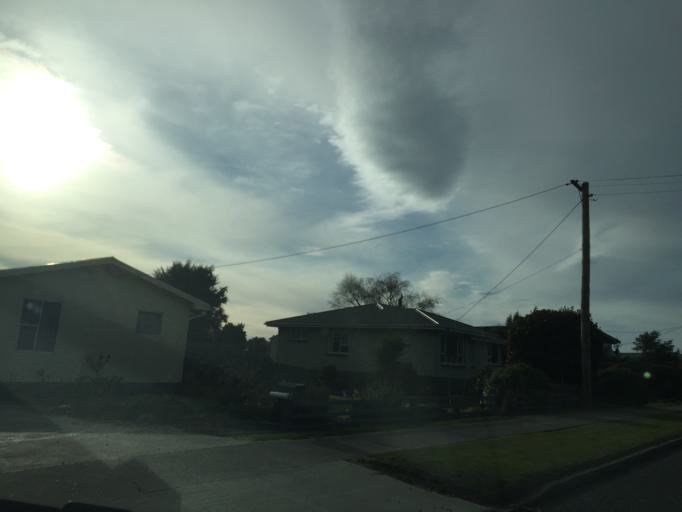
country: NZ
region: Southland
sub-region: Gore District
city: Gore
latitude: -46.1142
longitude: 168.9322
